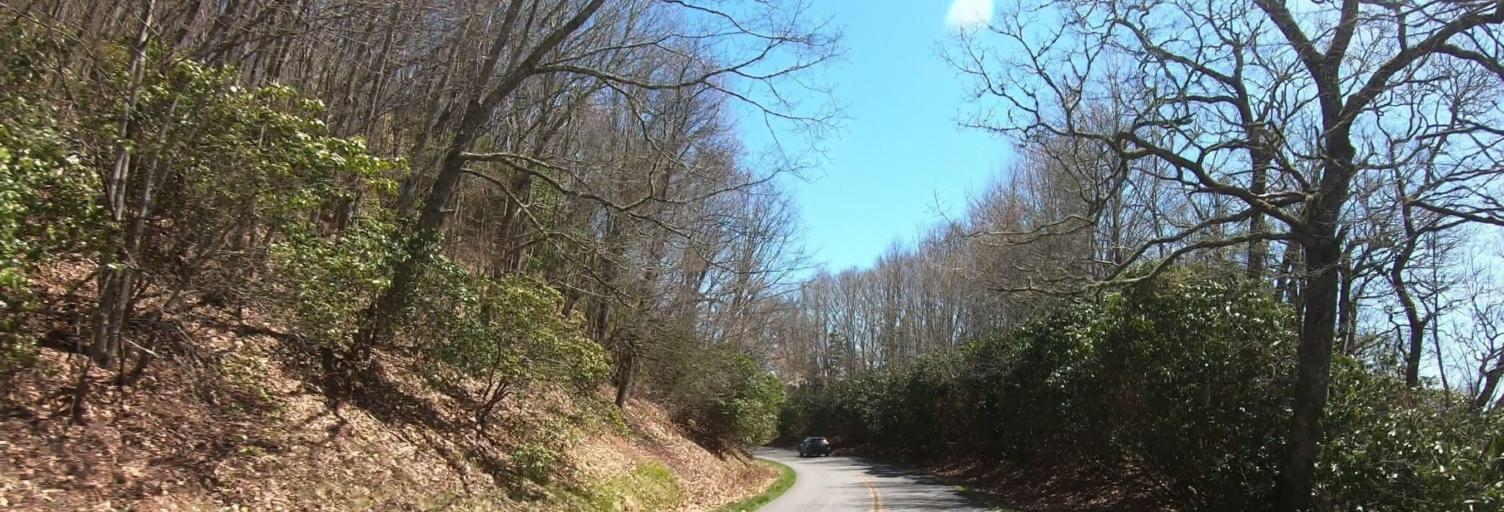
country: US
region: North Carolina
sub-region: Haywood County
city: Maggie Valley
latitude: 35.5087
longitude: -83.1834
